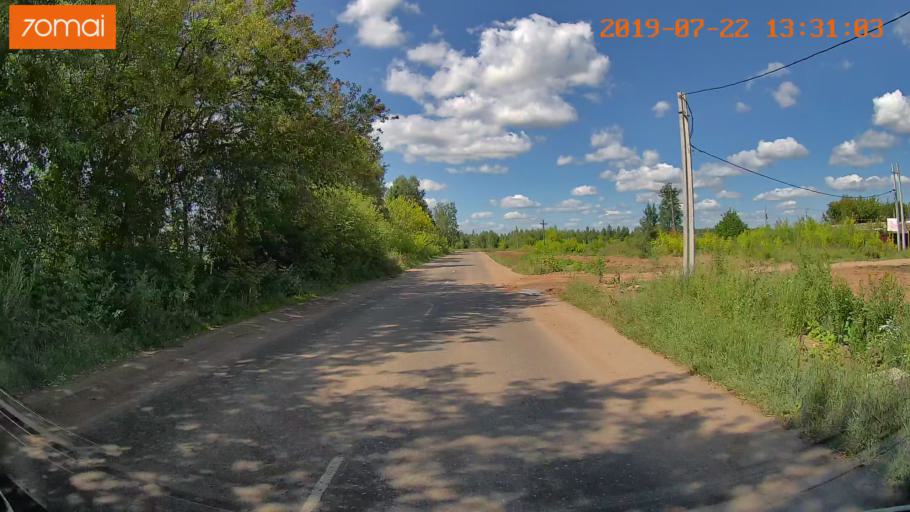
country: RU
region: Ivanovo
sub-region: Gorod Ivanovo
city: Ivanovo
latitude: 57.0559
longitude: 40.9209
